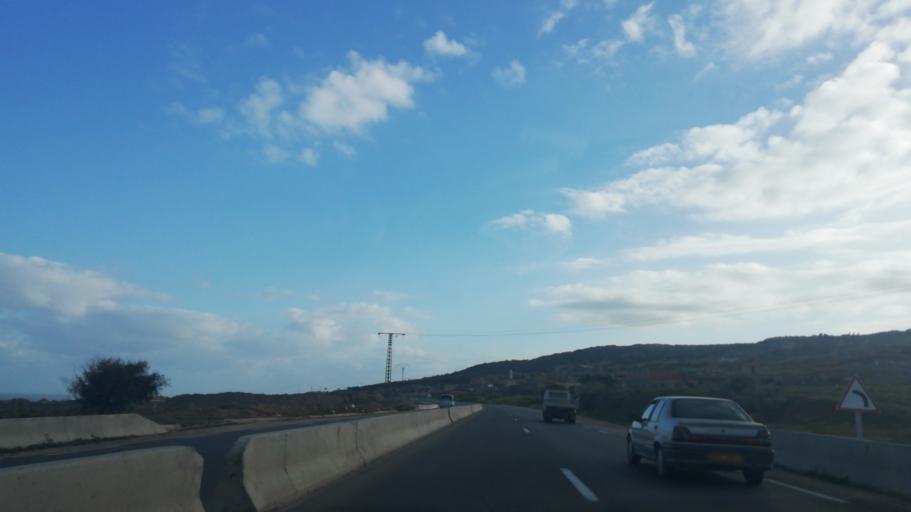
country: DZ
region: Mostaganem
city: Mostaganem
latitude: 36.0964
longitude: 0.2083
